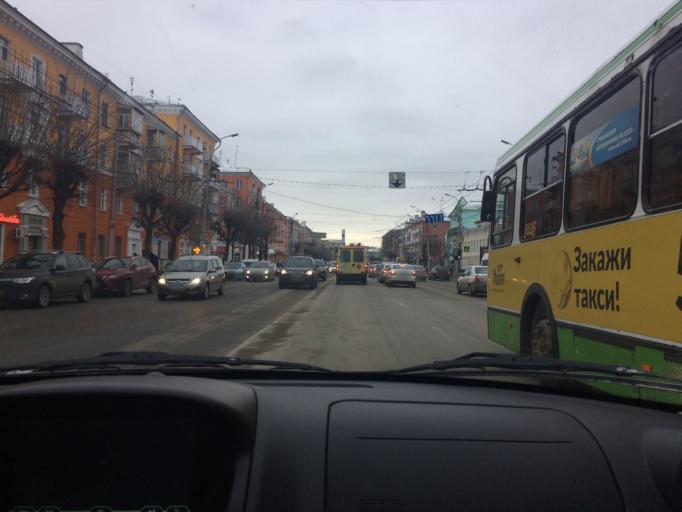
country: RU
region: Rjazan
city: Ryazan'
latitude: 54.6292
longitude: 39.7178
